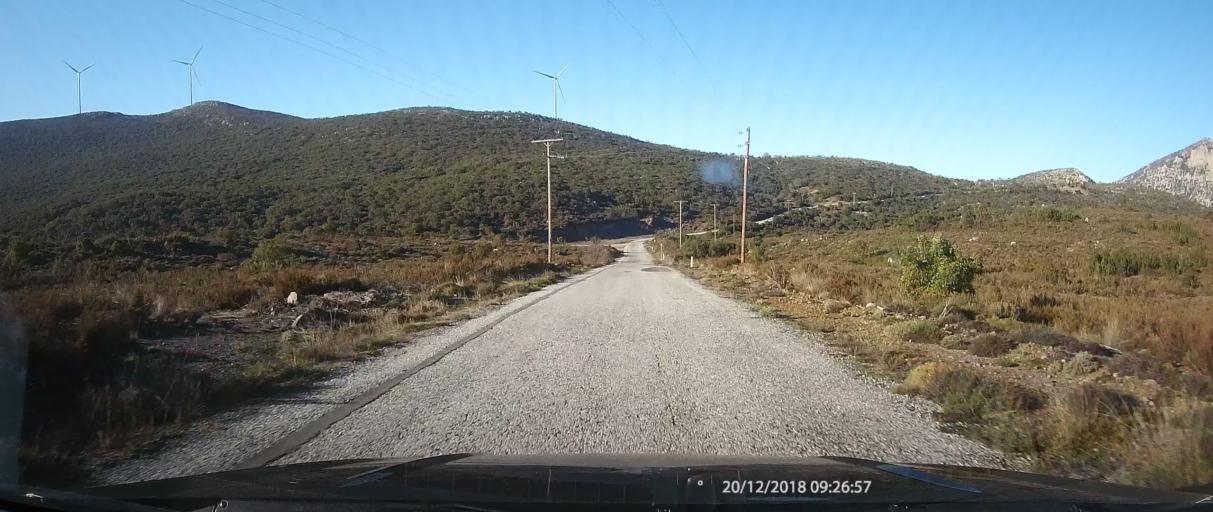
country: GR
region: Peloponnese
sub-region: Nomos Lakonias
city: Molaoi
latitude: 36.9594
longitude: 22.8707
